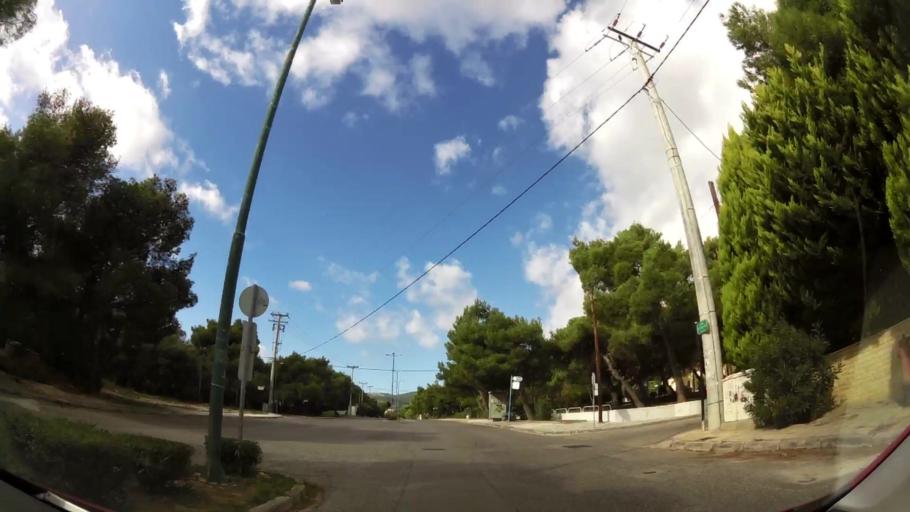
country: GR
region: Attica
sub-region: Nomarchia Anatolikis Attikis
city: Thrakomakedones
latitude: 38.1350
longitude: 23.7570
